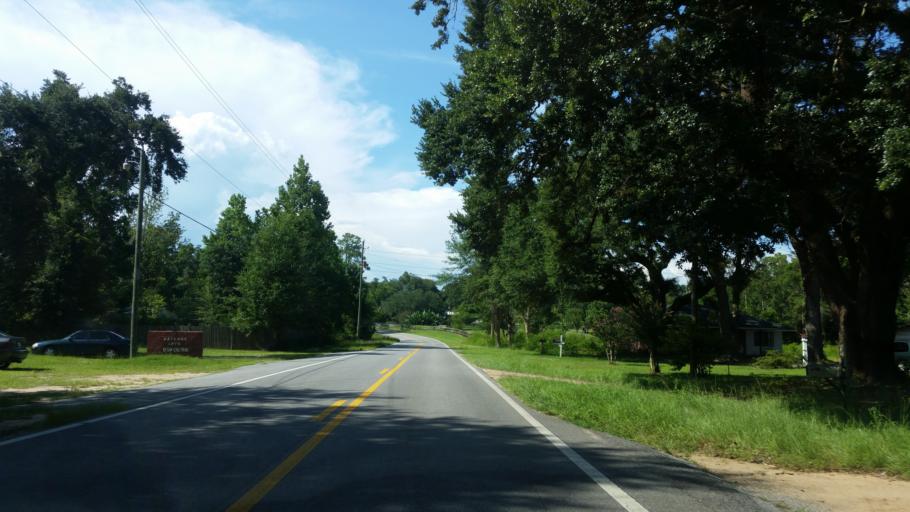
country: US
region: Florida
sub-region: Santa Rosa County
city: Pace
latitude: 30.5863
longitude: -87.1612
